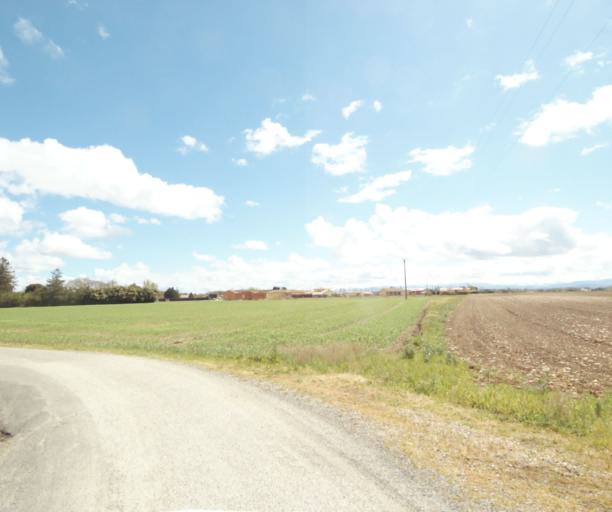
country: FR
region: Midi-Pyrenees
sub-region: Departement de l'Ariege
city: Saverdun
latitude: 43.2430
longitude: 1.6099
